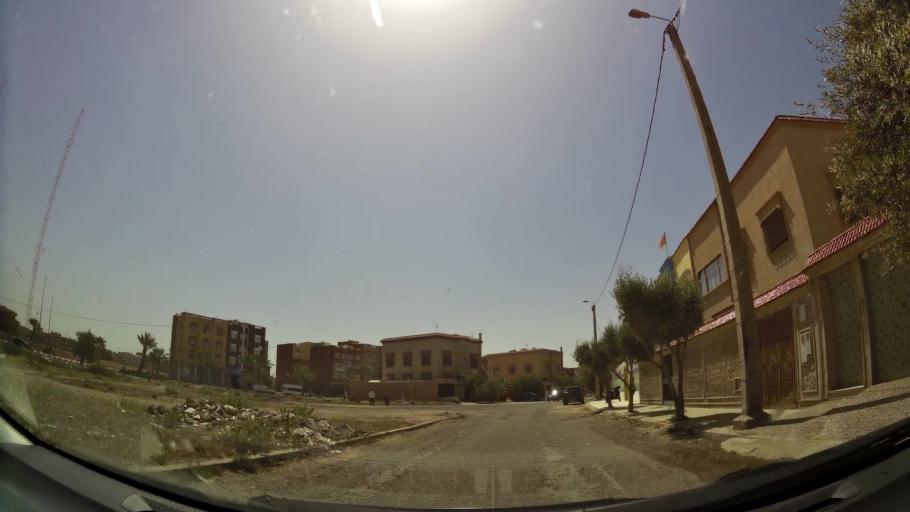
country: MA
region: Souss-Massa-Draa
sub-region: Inezgane-Ait Mellou
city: Inezgane
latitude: 30.3250
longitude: -9.5044
